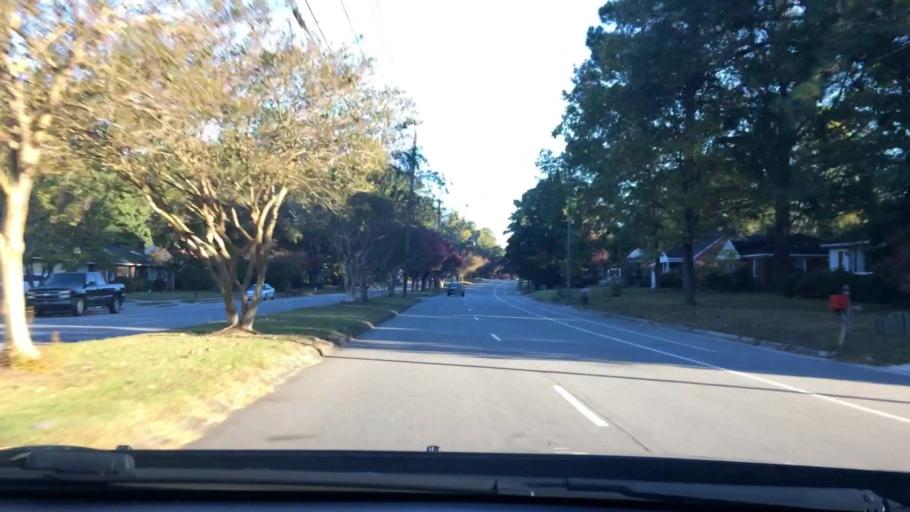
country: US
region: North Carolina
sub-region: Pitt County
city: Greenville
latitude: 35.5923
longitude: -77.3607
